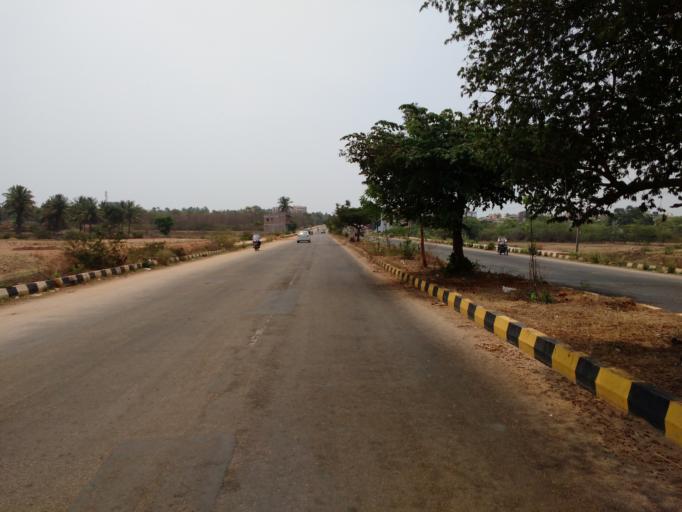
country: IN
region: Karnataka
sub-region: Hassan
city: Hassan
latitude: 13.0177
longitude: 76.1162
